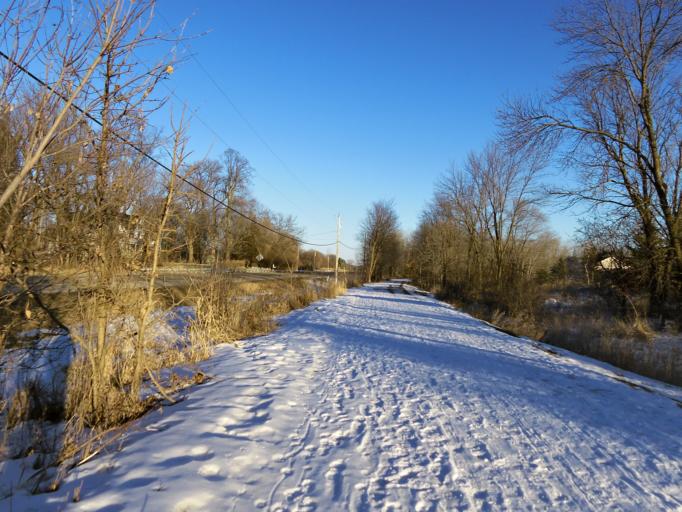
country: US
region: Minnesota
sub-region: Washington County
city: Stillwater
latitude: 45.0722
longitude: -92.8561
